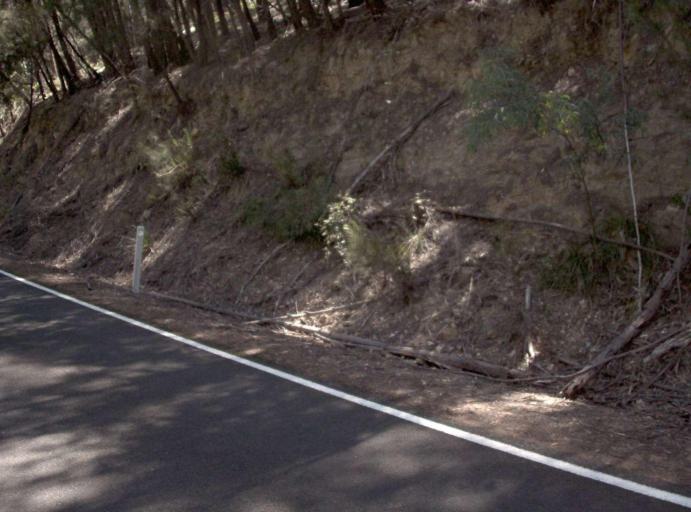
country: AU
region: Victoria
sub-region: East Gippsland
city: Lakes Entrance
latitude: -37.3755
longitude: 148.2176
